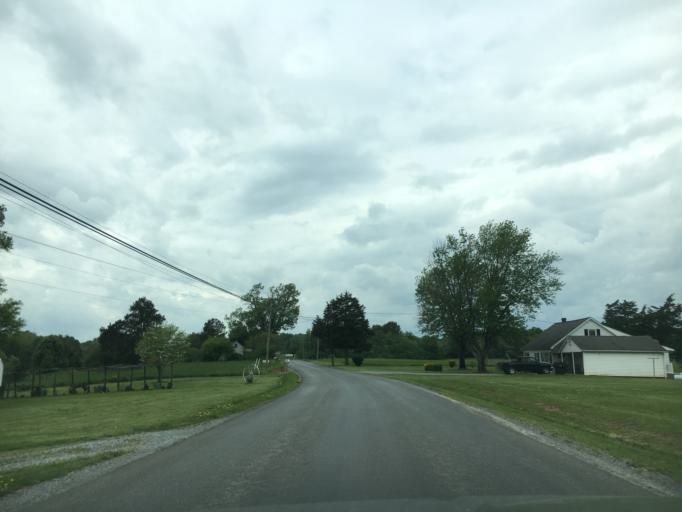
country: US
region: Virginia
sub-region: Campbell County
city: Rustburg
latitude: 37.1666
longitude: -79.0597
